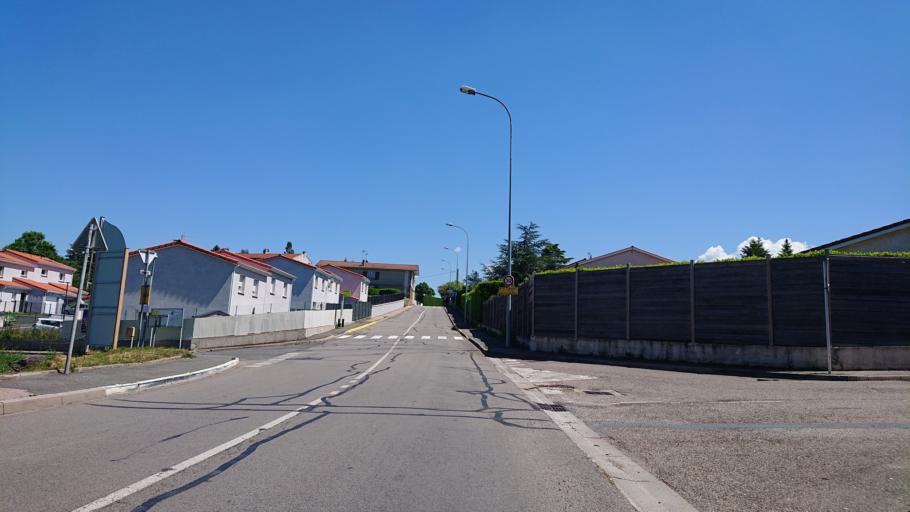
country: FR
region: Rhone-Alpes
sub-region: Departement de la Loire
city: Villars
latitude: 45.4540
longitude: 4.3568
